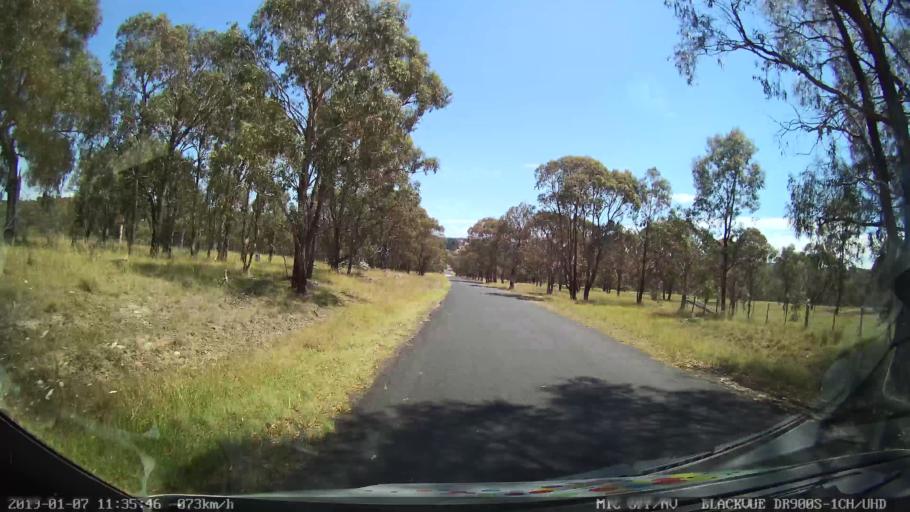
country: AU
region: New South Wales
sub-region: Armidale Dumaresq
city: Armidale
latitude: -30.3768
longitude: 151.5585
